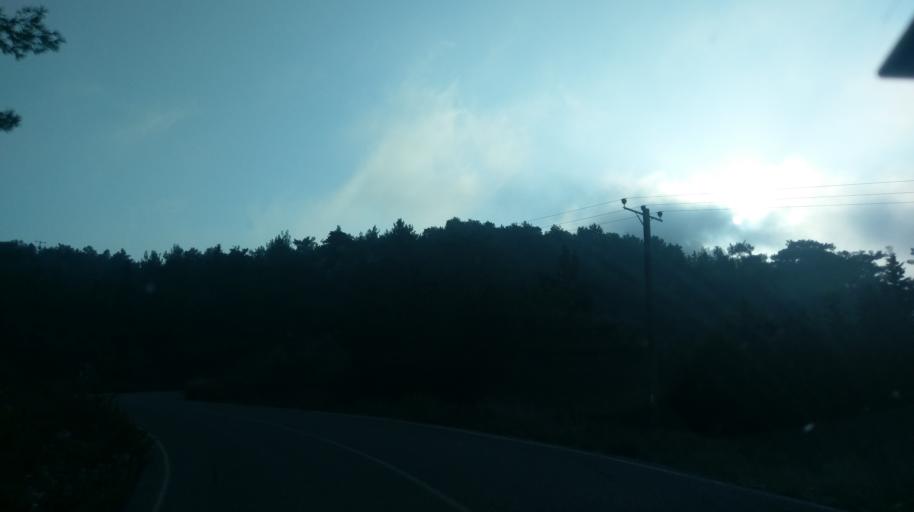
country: CY
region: Ammochostos
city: Trikomo
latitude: 35.3901
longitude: 33.8964
